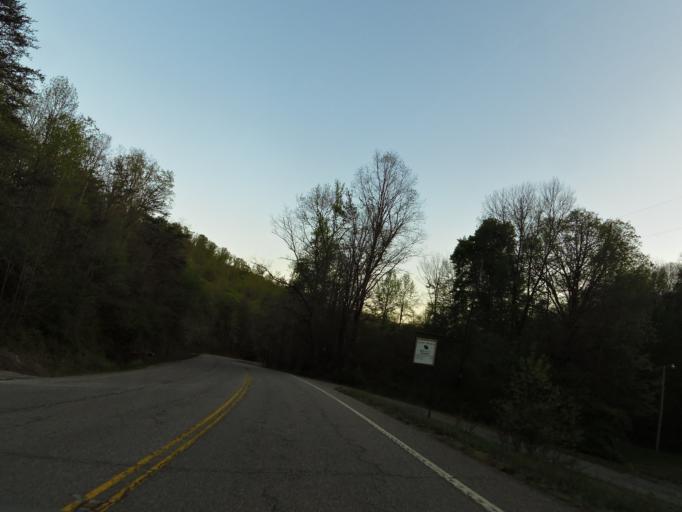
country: US
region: Tennessee
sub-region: Campbell County
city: Fincastle
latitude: 36.4512
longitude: -84.0762
